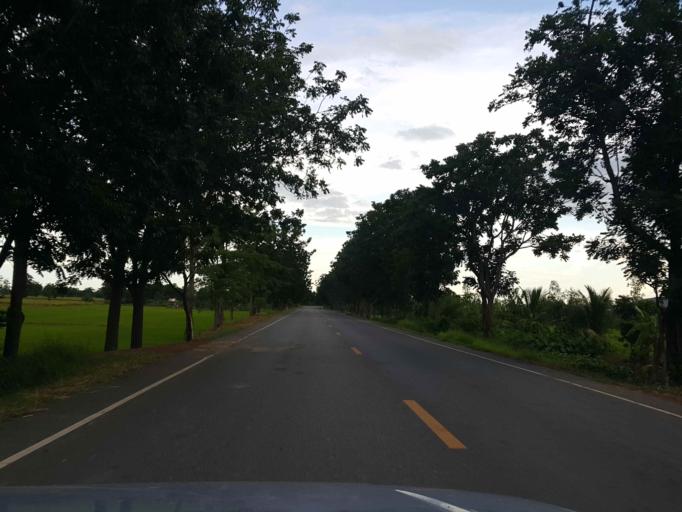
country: TH
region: Sukhothai
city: Sawankhalok
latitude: 17.3459
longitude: 99.7427
